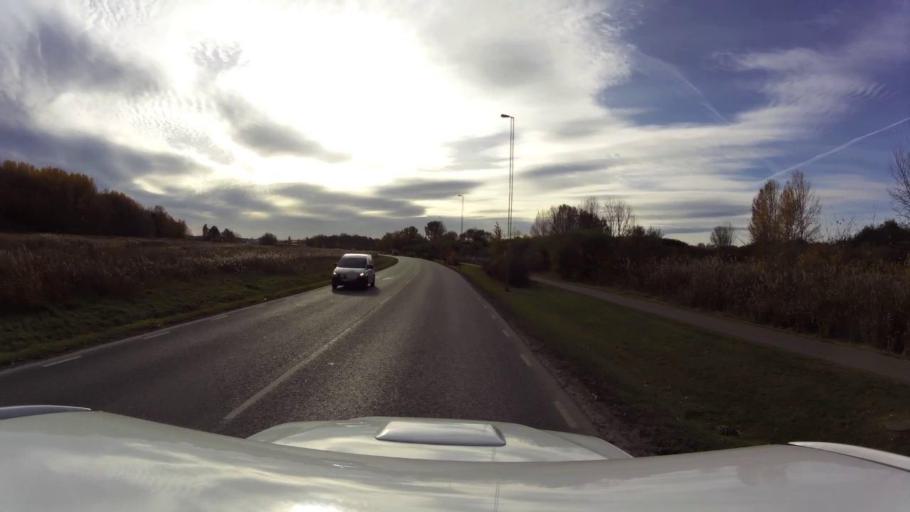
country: SE
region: OEstergoetland
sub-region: Linkopings Kommun
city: Linkoping
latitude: 58.4280
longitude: 15.6388
